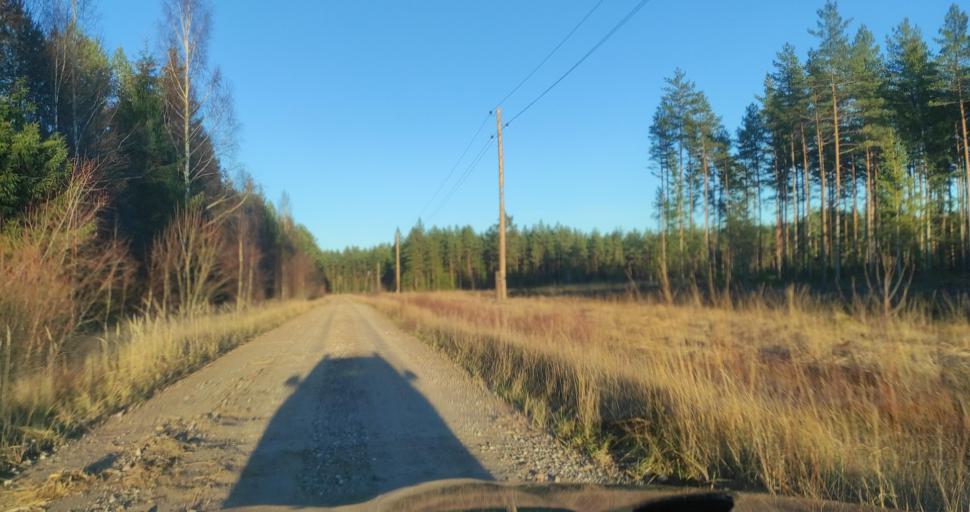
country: LV
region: Dundaga
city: Dundaga
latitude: 57.3709
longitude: 22.0742
